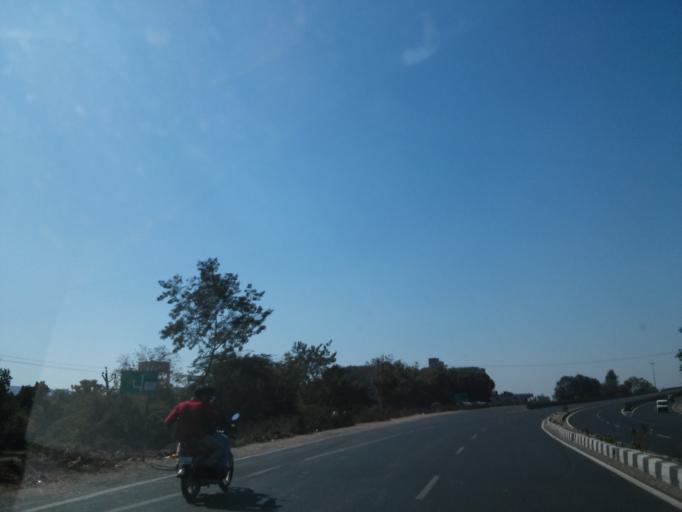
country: IN
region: Gujarat
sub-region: Sabar Kantha
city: Modasa
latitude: 23.6841
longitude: 73.3724
